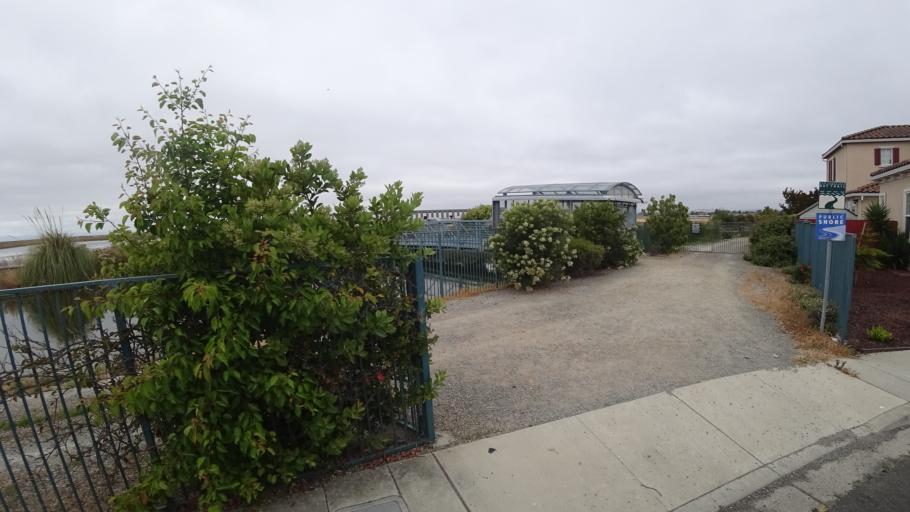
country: US
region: California
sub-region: Alameda County
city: Hayward
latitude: 37.6117
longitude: -122.0973
